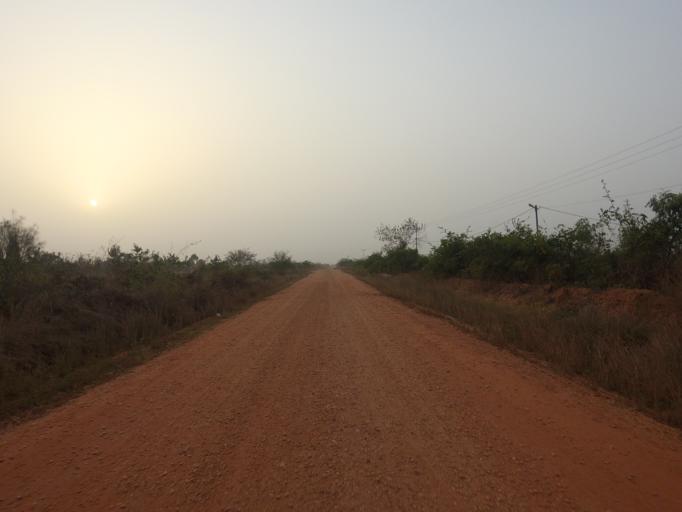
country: GH
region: Volta
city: Anloga
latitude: 5.9713
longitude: 0.6214
